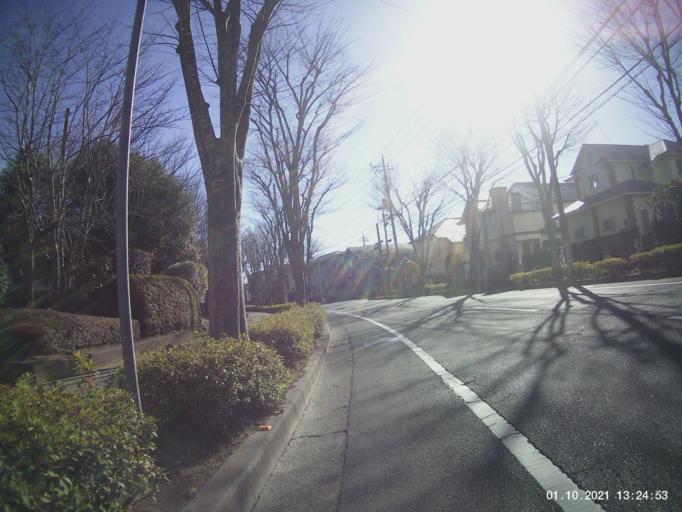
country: JP
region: Chiba
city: Yotsukaido
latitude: 35.6069
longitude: 140.2052
